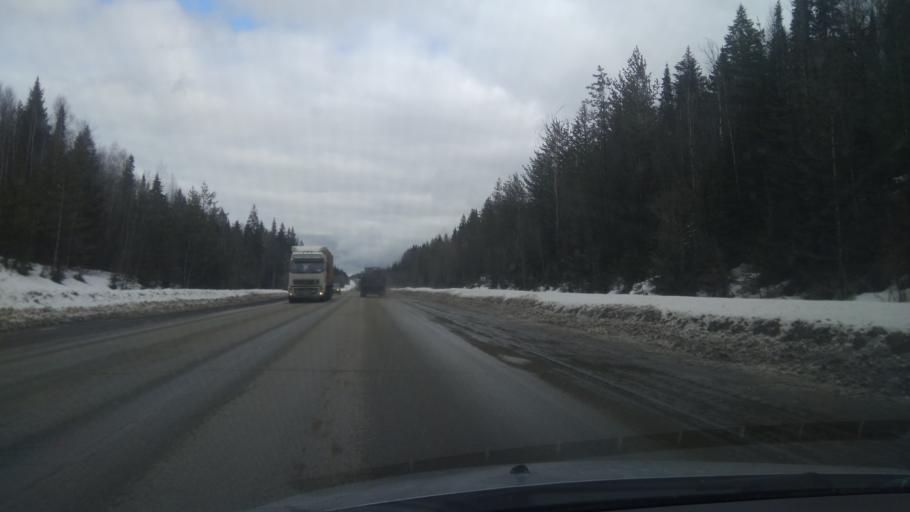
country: RU
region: Sverdlovsk
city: Bisert'
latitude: 56.8269
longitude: 59.2144
